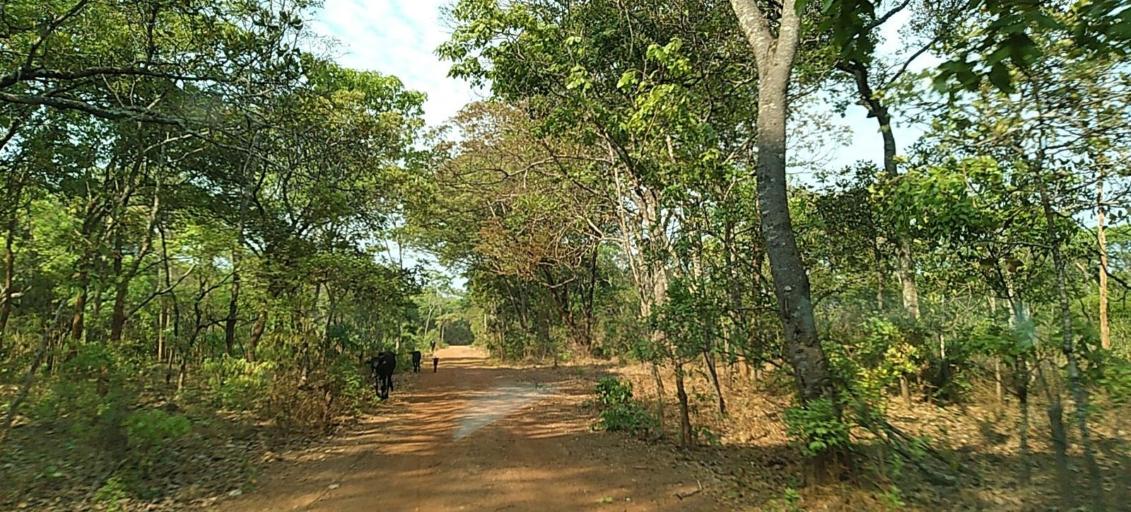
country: ZM
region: Copperbelt
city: Kalulushi
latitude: -12.9975
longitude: 27.7101
